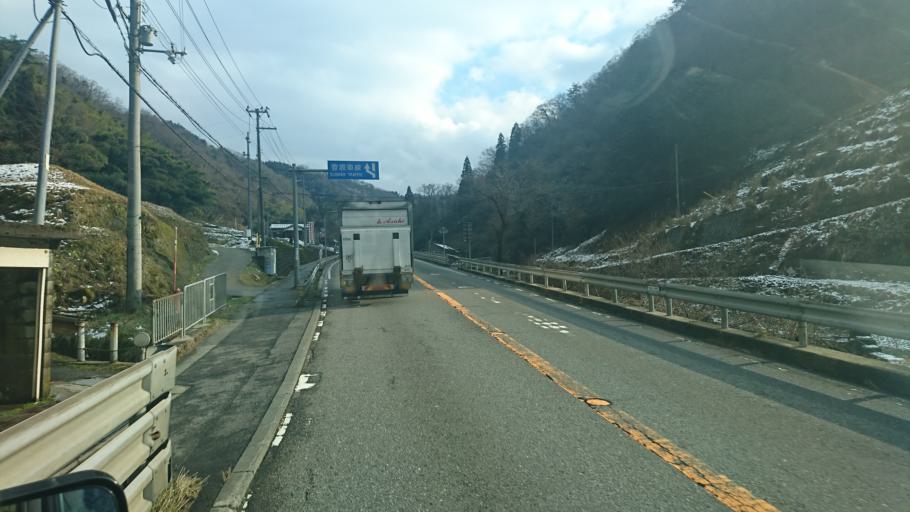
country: JP
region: Tottori
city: Tottori
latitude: 35.5240
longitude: 134.5210
